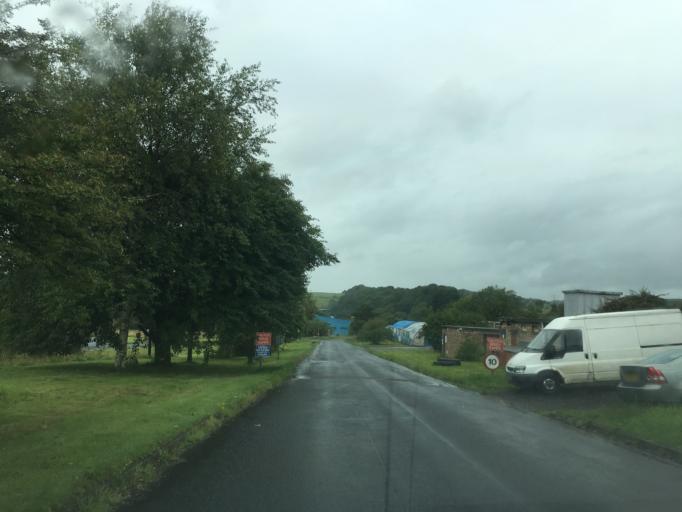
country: GB
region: Scotland
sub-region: Fife
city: Townhill
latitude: 56.1139
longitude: -3.4498
